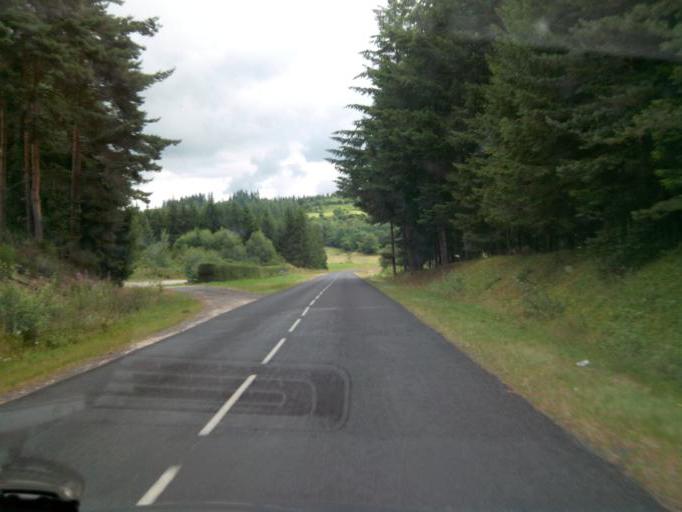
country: FR
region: Rhone-Alpes
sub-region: Departement de la Loire
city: Usson-en-Forez
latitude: 45.3905
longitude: 3.9696
